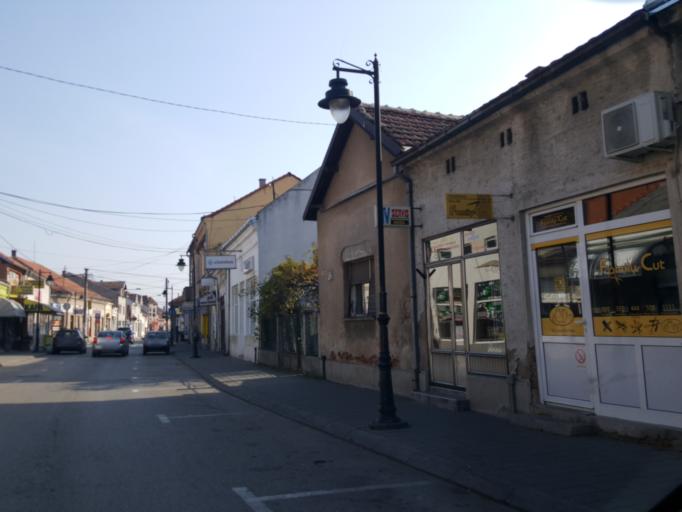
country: RS
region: Central Serbia
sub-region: Borski Okrug
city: Negotin
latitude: 44.2260
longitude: 22.5322
